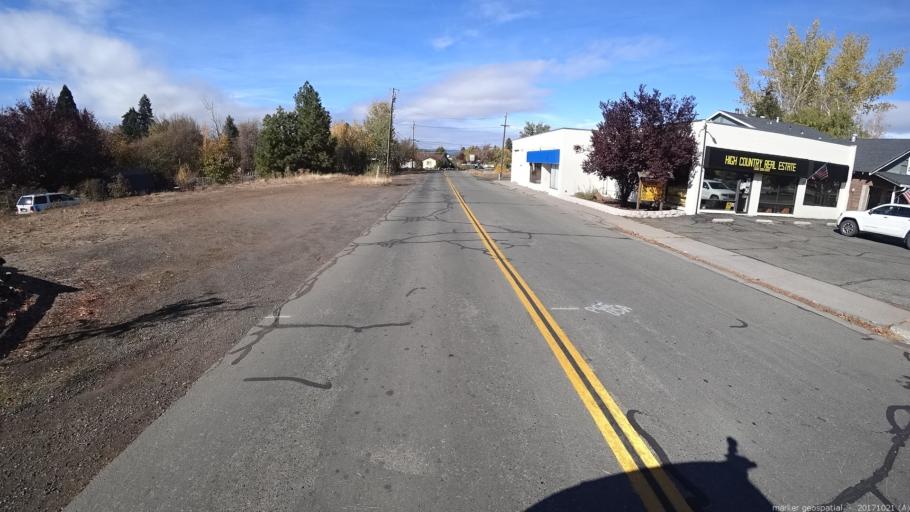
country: US
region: California
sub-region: Shasta County
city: Burney
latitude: 40.8826
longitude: -121.6617
